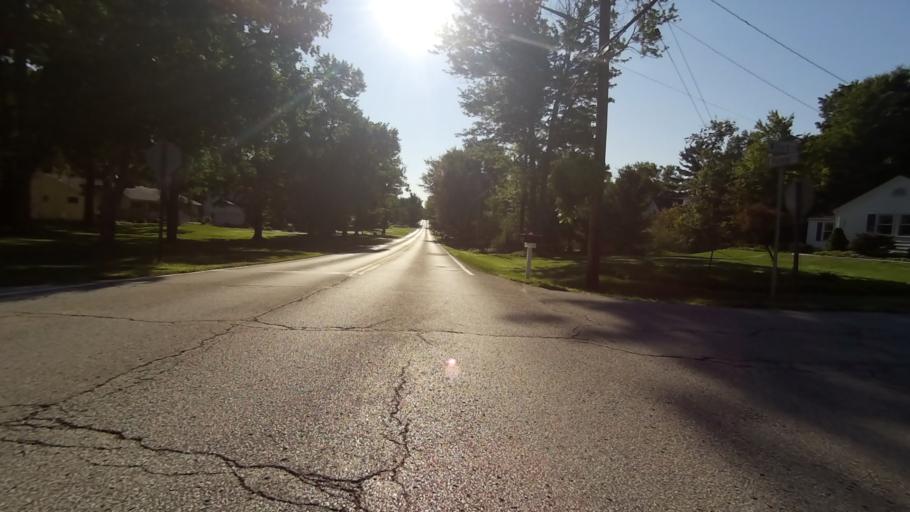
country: US
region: Ohio
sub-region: Portage County
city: Aurora
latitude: 41.3111
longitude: -81.3412
